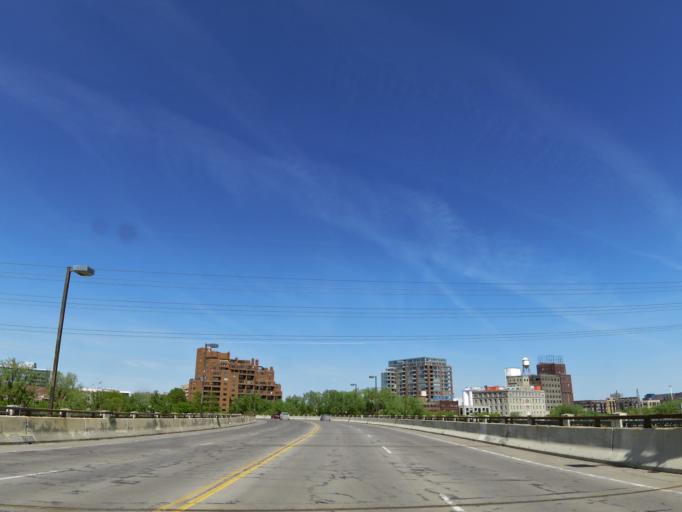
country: US
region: Minnesota
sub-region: Hennepin County
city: Minneapolis
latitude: 44.9834
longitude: -93.2586
